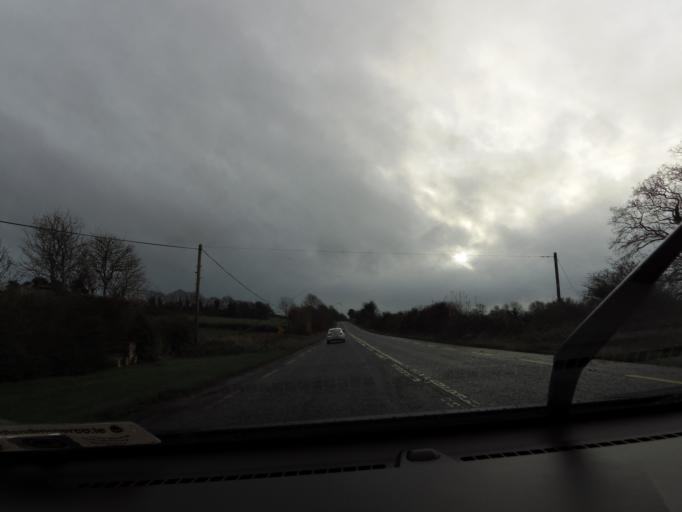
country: IE
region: Munster
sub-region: North Tipperary
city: Roscrea
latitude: 52.9854
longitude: -7.8517
